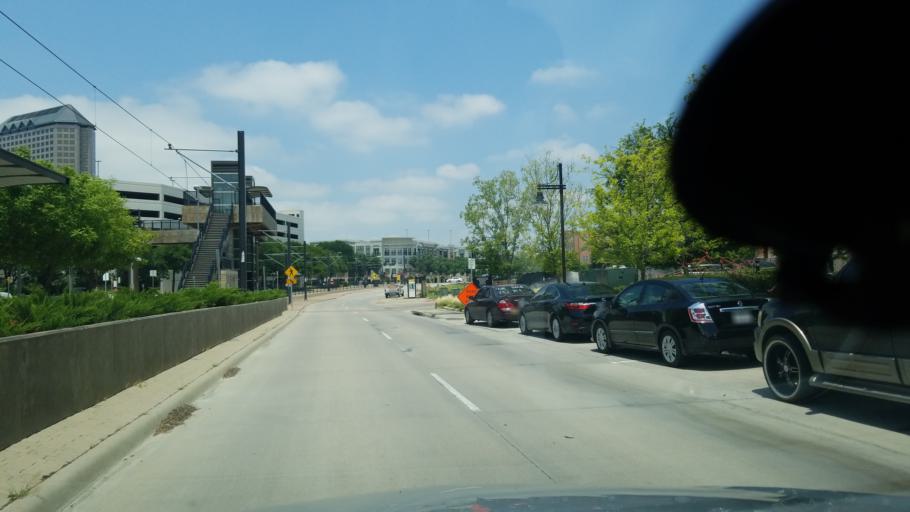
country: US
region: Texas
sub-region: Dallas County
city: Irving
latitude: 32.8688
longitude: -96.9336
